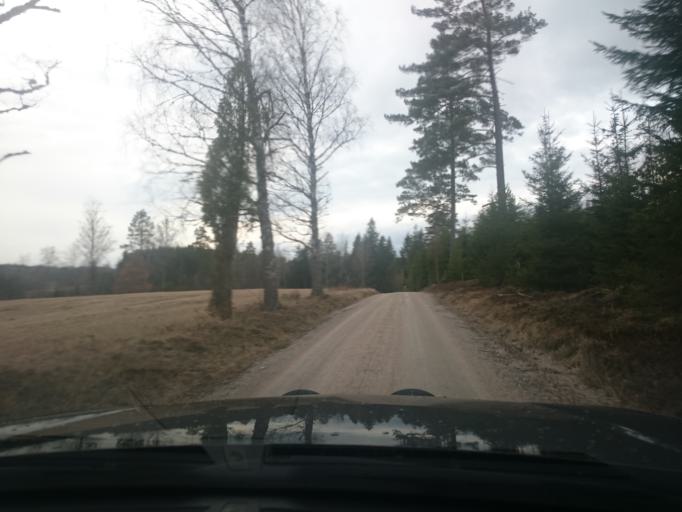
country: SE
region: Joenkoeping
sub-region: Vetlanda Kommun
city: Vetlanda
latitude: 57.2843
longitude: 15.1723
